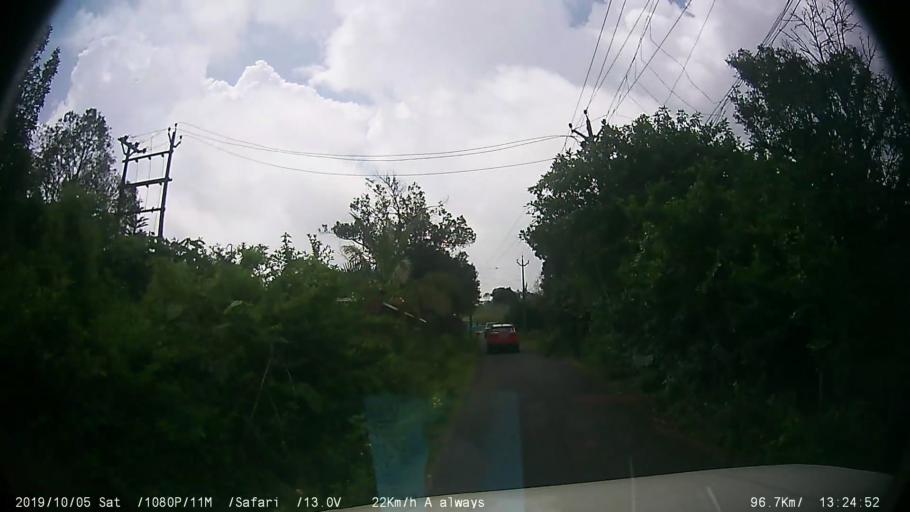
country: IN
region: Kerala
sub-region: Kottayam
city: Erattupetta
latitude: 9.5762
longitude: 76.9715
